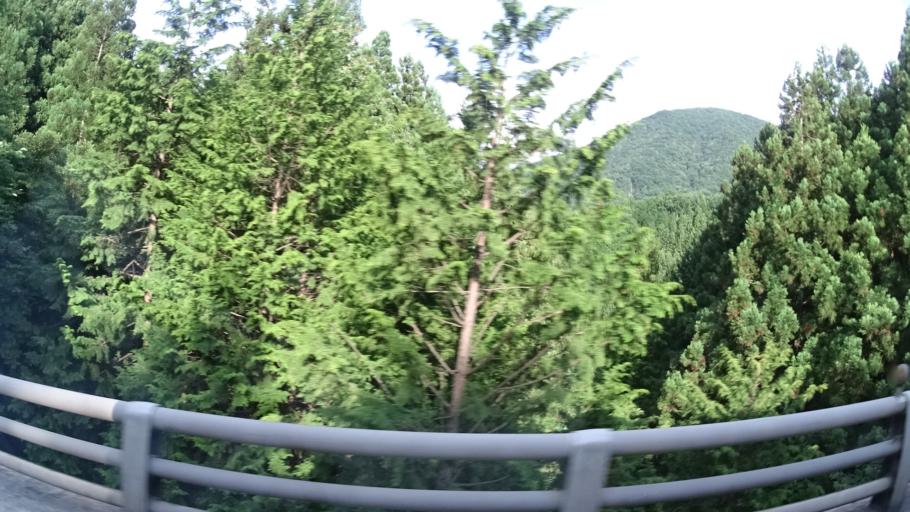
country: JP
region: Tochigi
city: Nikko
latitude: 36.7213
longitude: 139.5344
